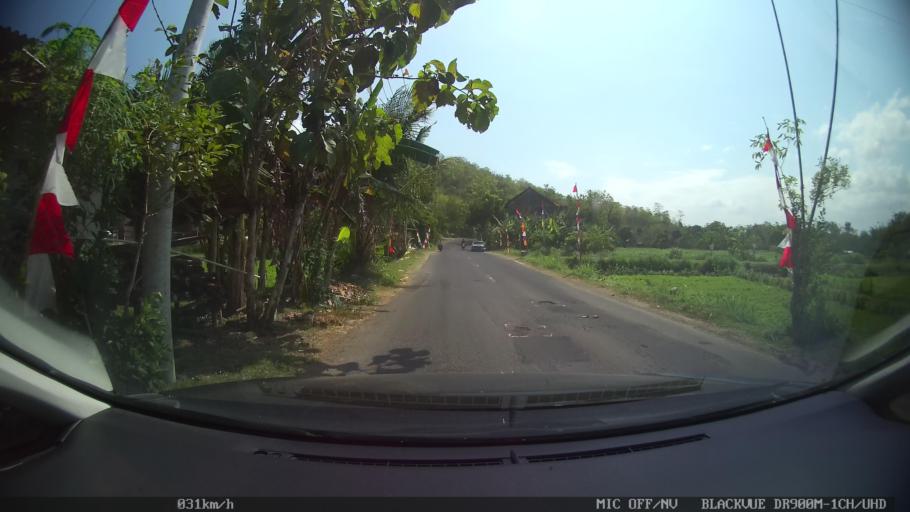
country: ID
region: Daerah Istimewa Yogyakarta
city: Pundong
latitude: -7.9600
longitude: 110.3775
